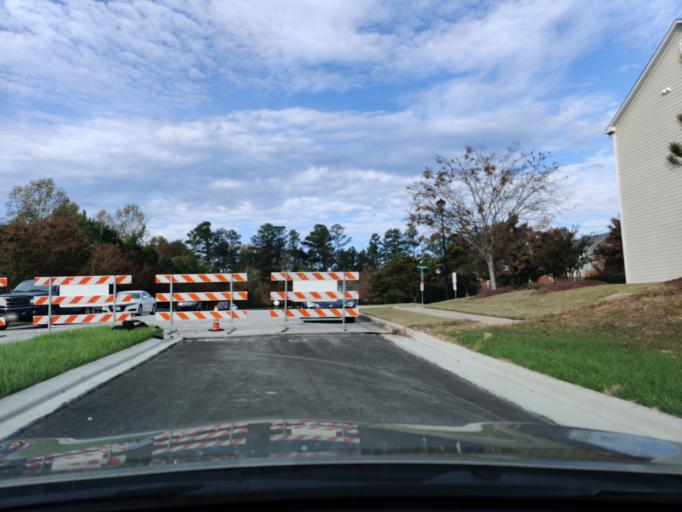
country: US
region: North Carolina
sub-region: Wake County
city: Morrisville
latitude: 35.8281
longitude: -78.8594
